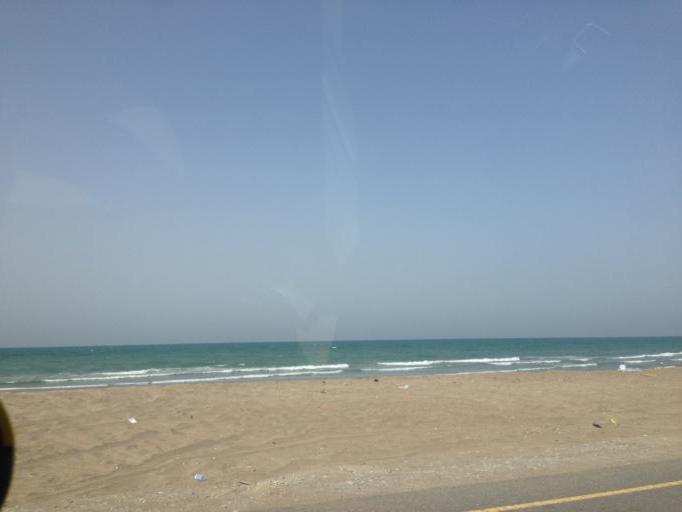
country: OM
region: Al Batinah
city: Barka'
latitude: 23.7272
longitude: 57.8425
